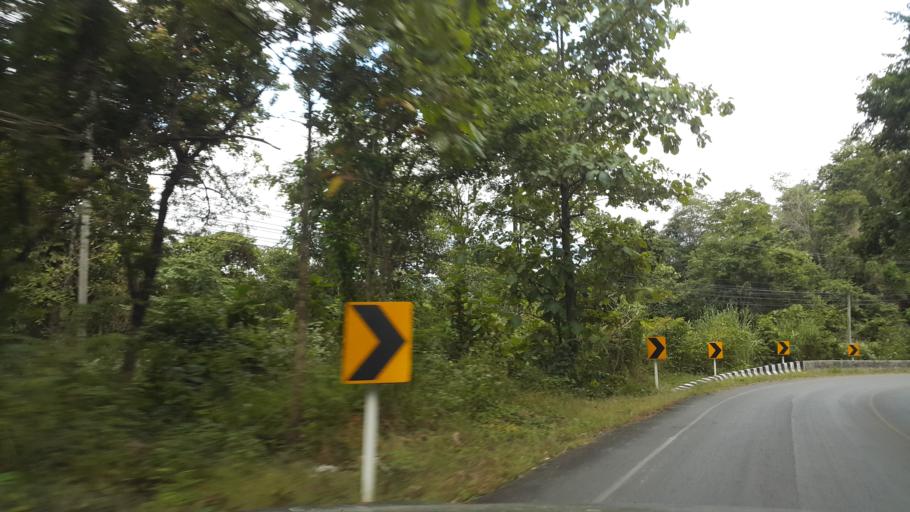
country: TH
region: Lampang
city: Thoen
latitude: 17.6175
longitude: 99.3206
